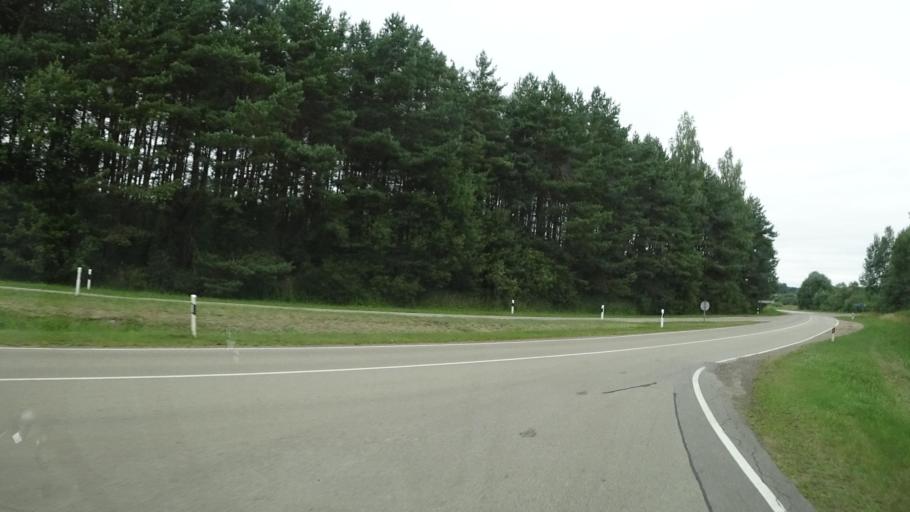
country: LT
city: Kelme
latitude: 55.3993
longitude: 22.8666
